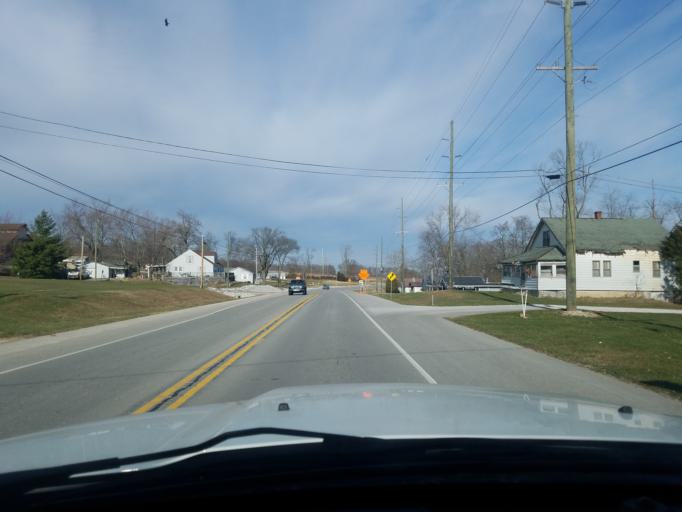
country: US
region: Indiana
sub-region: Orange County
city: Paoli
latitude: 38.5780
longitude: -86.4581
